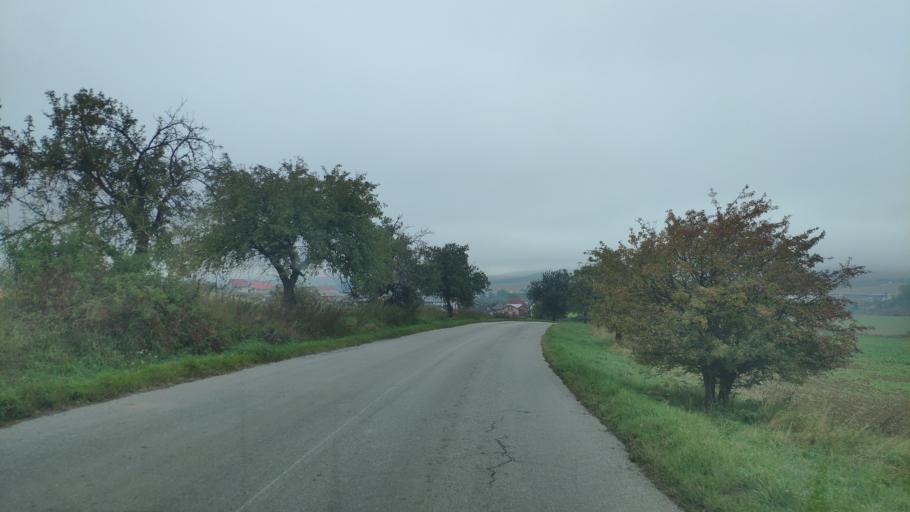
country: SK
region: Kosicky
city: Kosice
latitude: 48.8179
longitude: 21.4038
